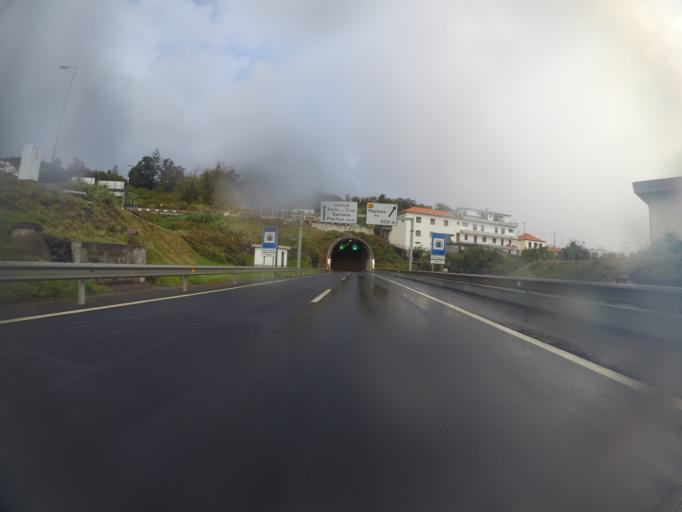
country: PT
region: Madeira
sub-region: Machico
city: Machico
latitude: 32.7071
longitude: -16.7665
